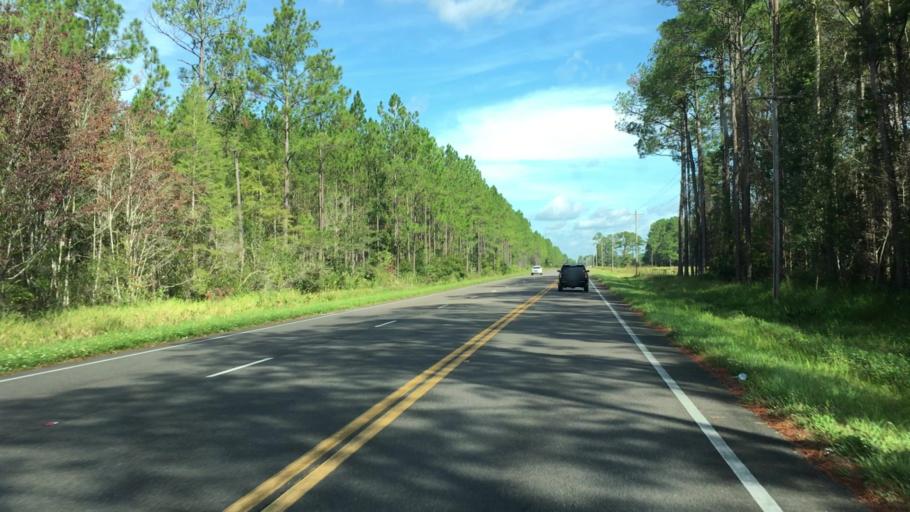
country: US
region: Florida
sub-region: Alachua County
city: Gainesville
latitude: 29.7474
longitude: -82.2773
